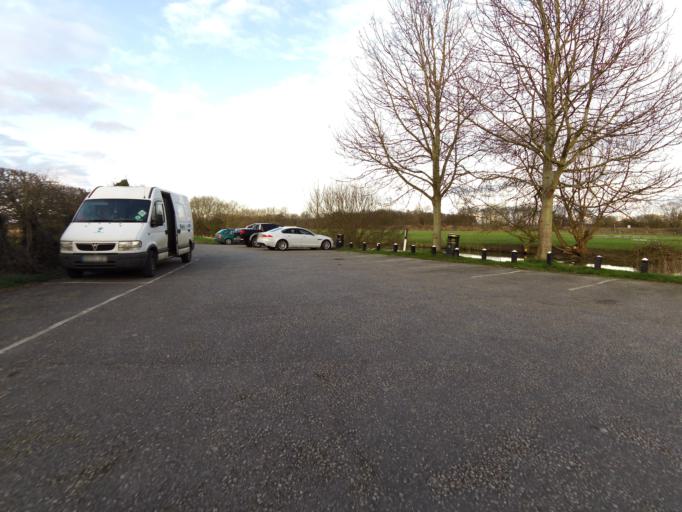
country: GB
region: England
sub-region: North Yorkshire
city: Brayton
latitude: 53.7657
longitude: -1.0761
